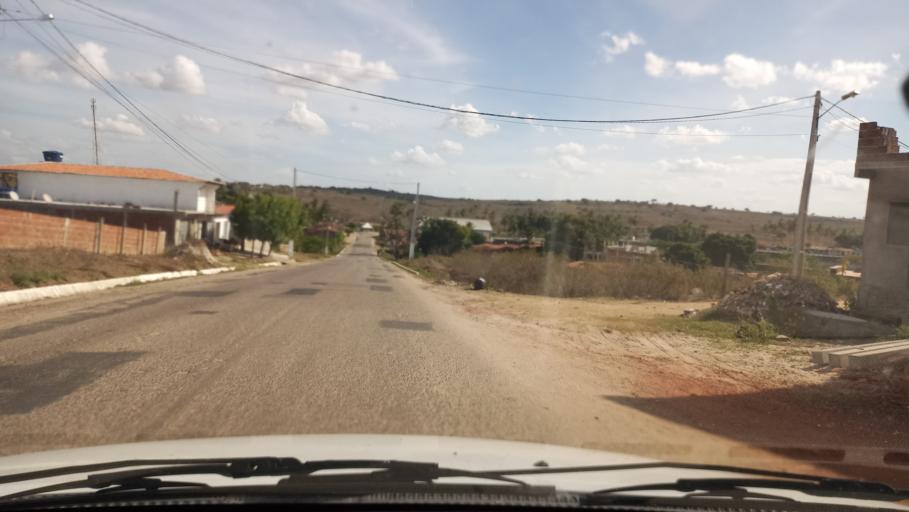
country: BR
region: Rio Grande do Norte
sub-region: Goianinha
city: Goianinha
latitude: -6.3276
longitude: -35.3044
